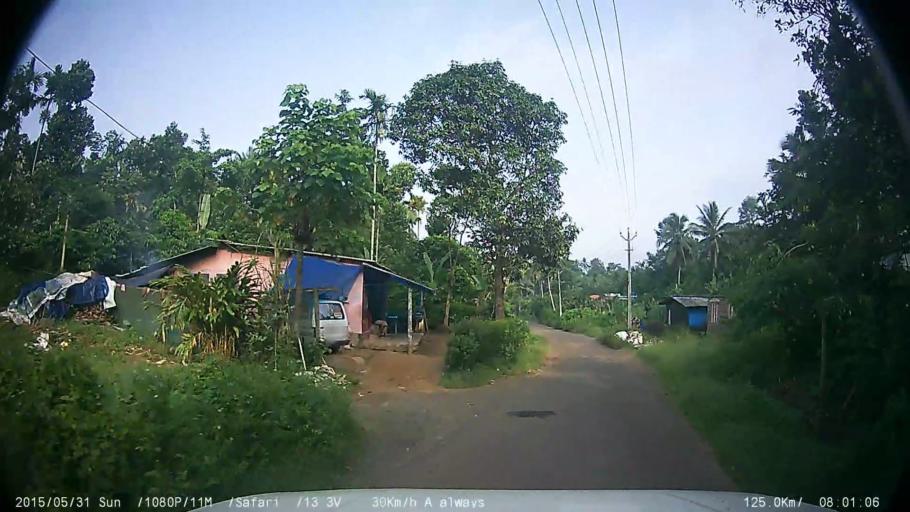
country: IN
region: Kerala
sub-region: Wayanad
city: Kalpetta
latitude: 11.6320
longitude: 76.0484
